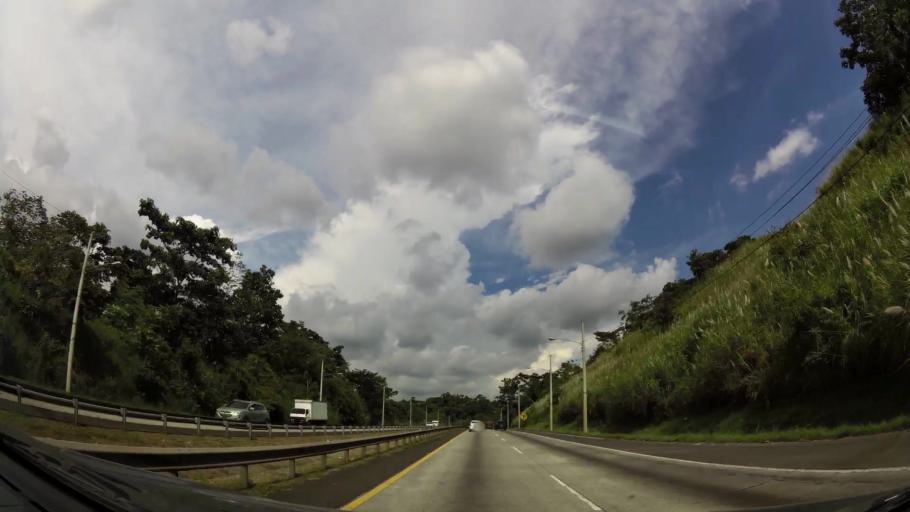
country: PA
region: Panama
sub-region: Distrito de Panama
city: Paraiso
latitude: 9.0387
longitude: -79.5723
